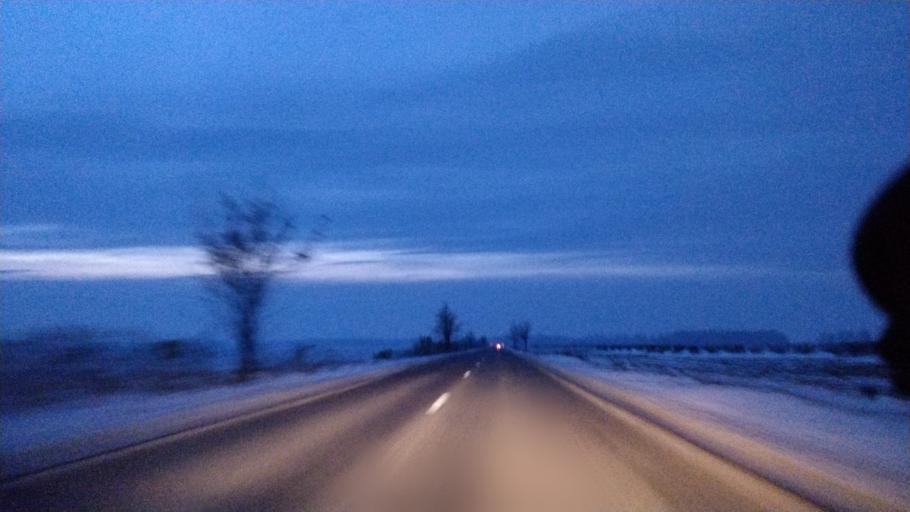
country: RO
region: Vrancea
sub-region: Comuna Suraia
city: Suraia
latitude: 45.6427
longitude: 27.3622
